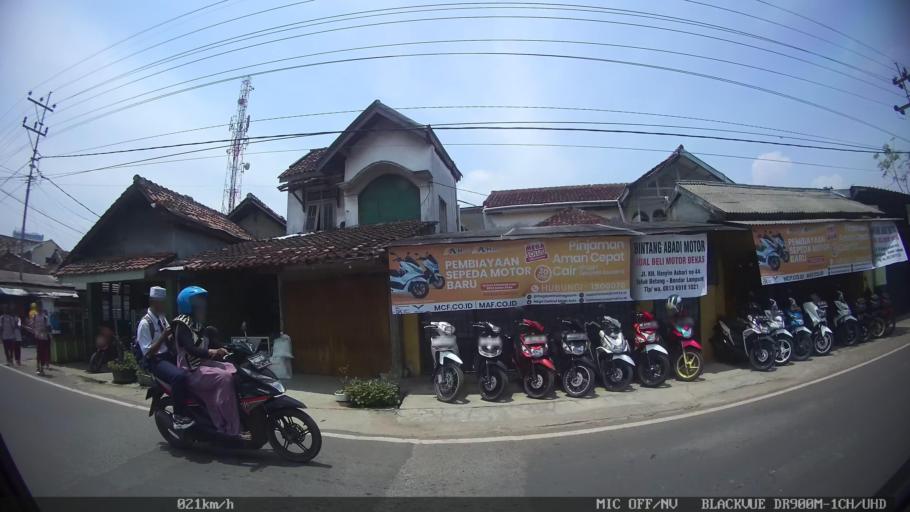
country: ID
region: Lampung
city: Bandarlampung
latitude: -5.4469
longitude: 105.2561
